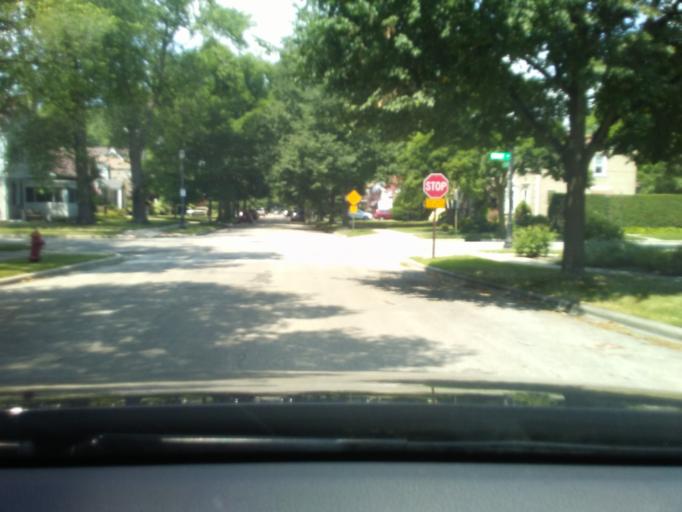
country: US
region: Illinois
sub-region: Cook County
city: Evanston
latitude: 42.0299
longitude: -87.6921
